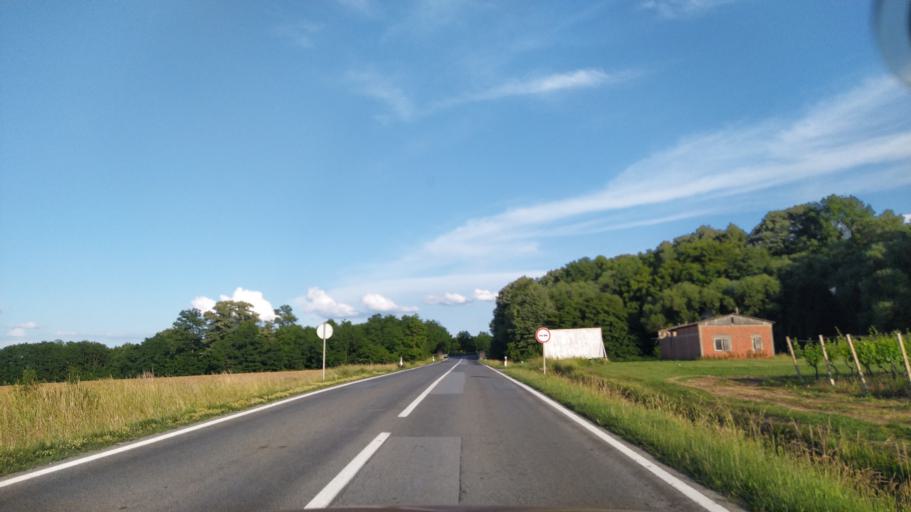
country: HR
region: Virovitick-Podravska
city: Slatina
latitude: 45.6728
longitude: 17.7585
